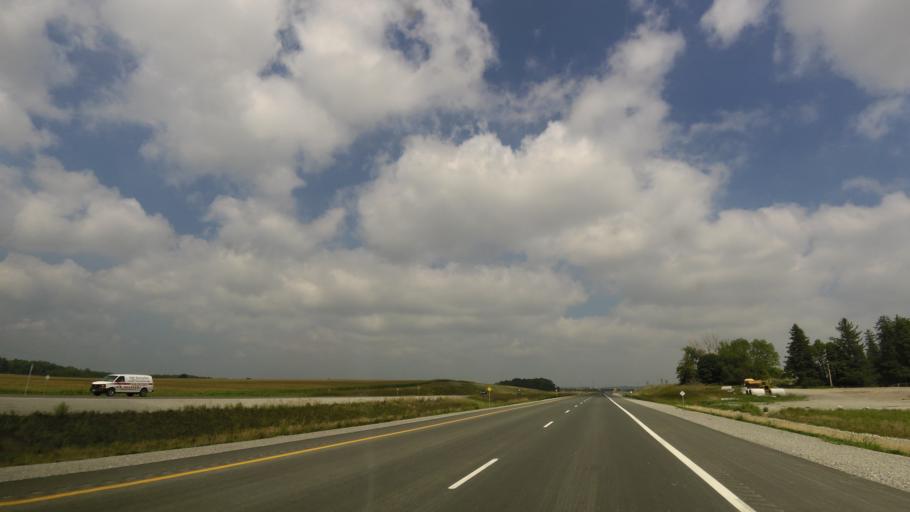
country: CA
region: Ontario
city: Oshawa
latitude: 43.9642
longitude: -78.9178
